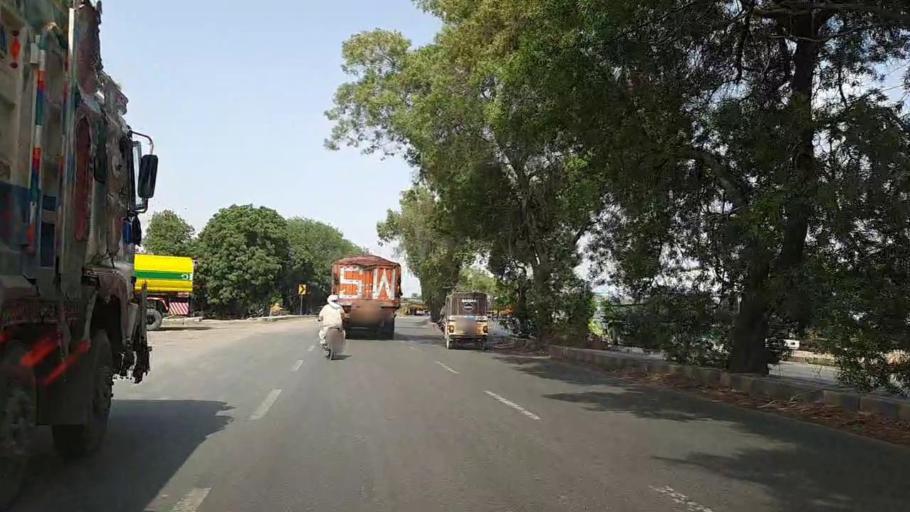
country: PK
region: Sindh
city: Malir Cantonment
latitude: 24.8670
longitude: 67.3034
